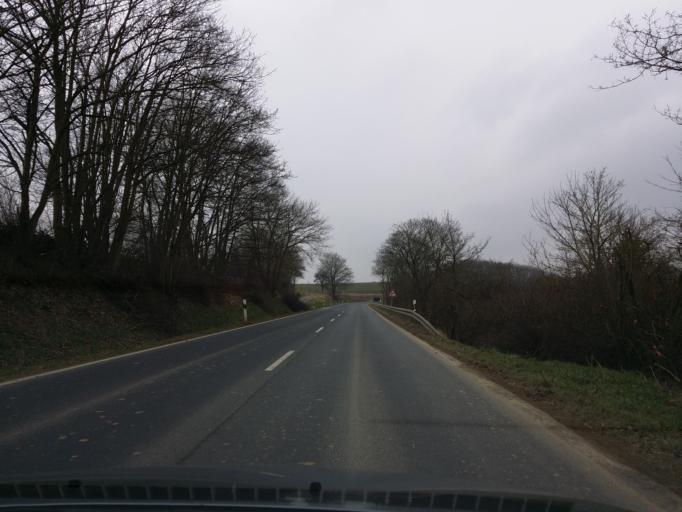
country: DE
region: Hesse
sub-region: Regierungsbezirk Darmstadt
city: Waldems
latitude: 50.2473
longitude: 8.3117
